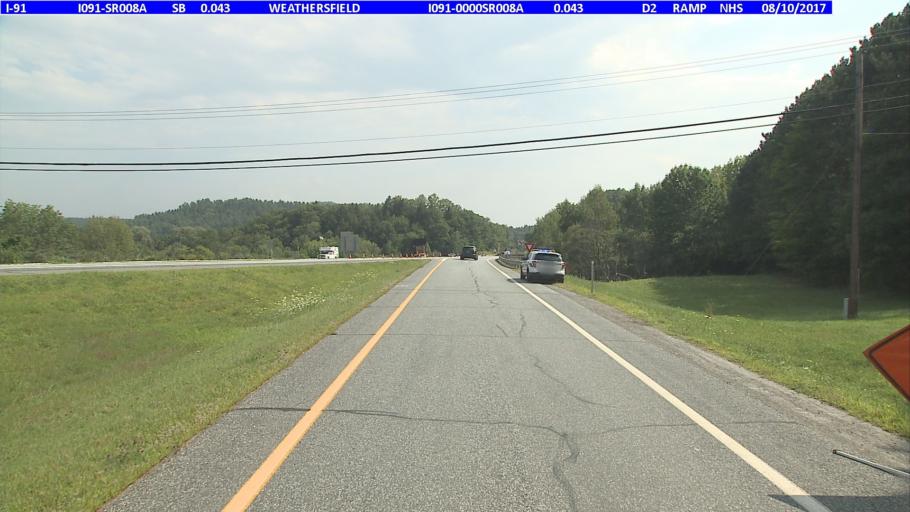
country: US
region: New Hampshire
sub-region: Sullivan County
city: Claremont
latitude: 43.4015
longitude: -72.4149
